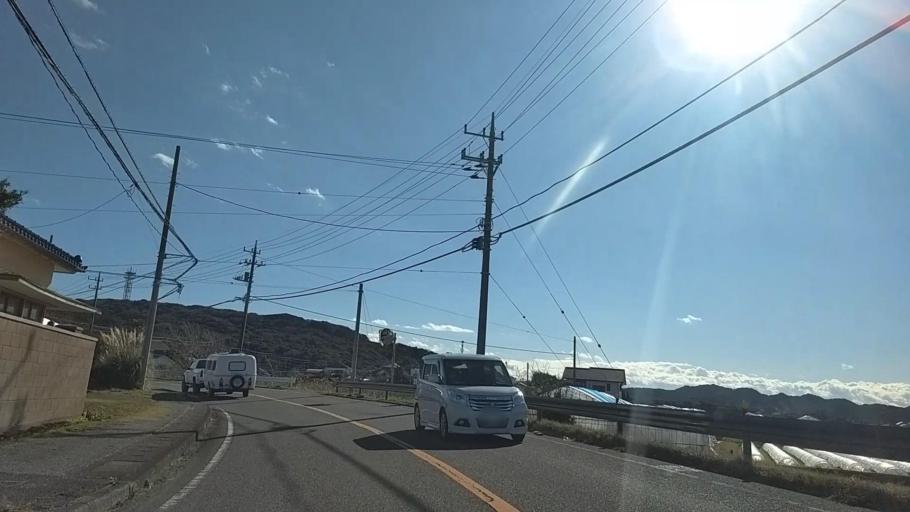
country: JP
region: Chiba
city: Tateyama
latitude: 34.9421
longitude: 139.8378
